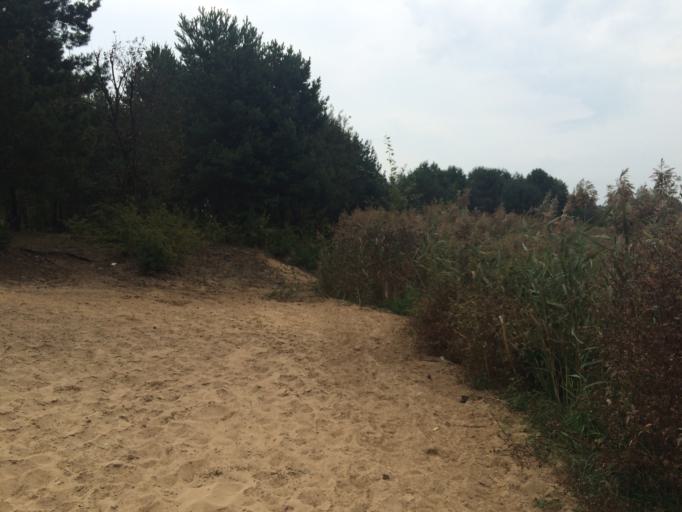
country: PL
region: Swietokrzyskie
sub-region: Powiat starachowicki
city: Starachowice
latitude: 51.0274
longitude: 21.0405
